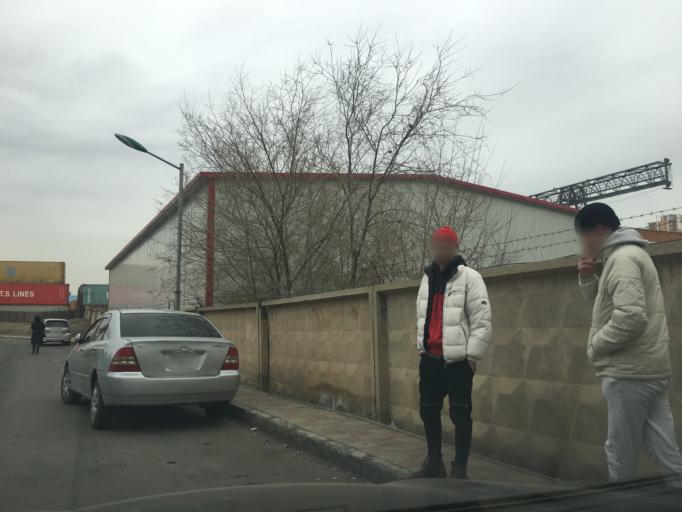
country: MN
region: Ulaanbaatar
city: Ulaanbaatar
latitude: 47.9039
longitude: 106.8899
